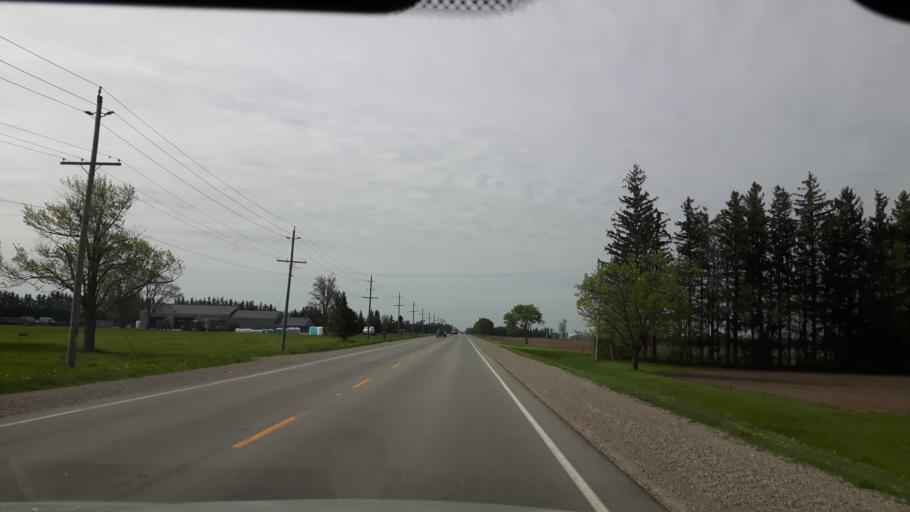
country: CA
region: Ontario
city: South Huron
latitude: 43.4049
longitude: -81.4926
